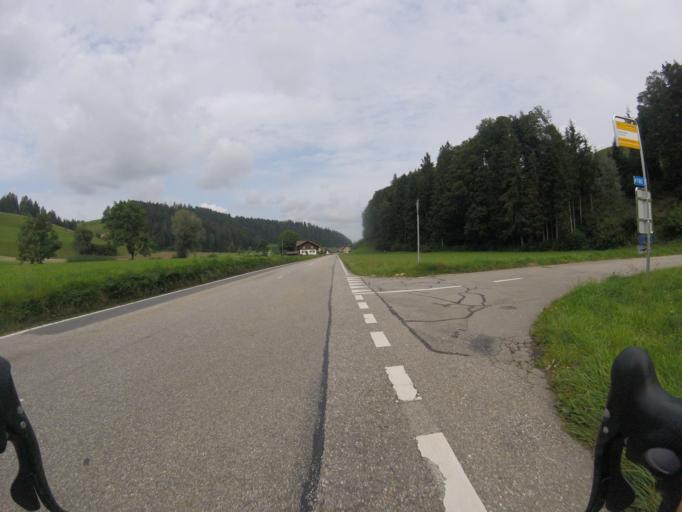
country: CH
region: Bern
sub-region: Emmental District
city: Lutzelfluh
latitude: 46.9921
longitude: 7.6877
